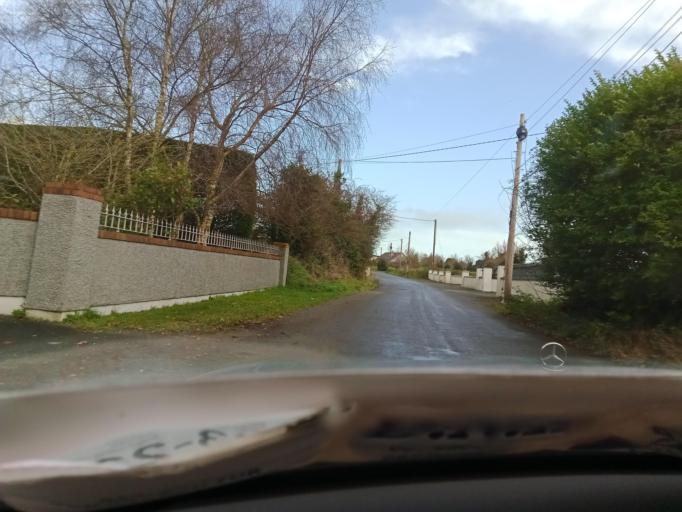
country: IE
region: Leinster
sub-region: Kilkenny
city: Mooncoin
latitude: 52.2875
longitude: -7.2531
